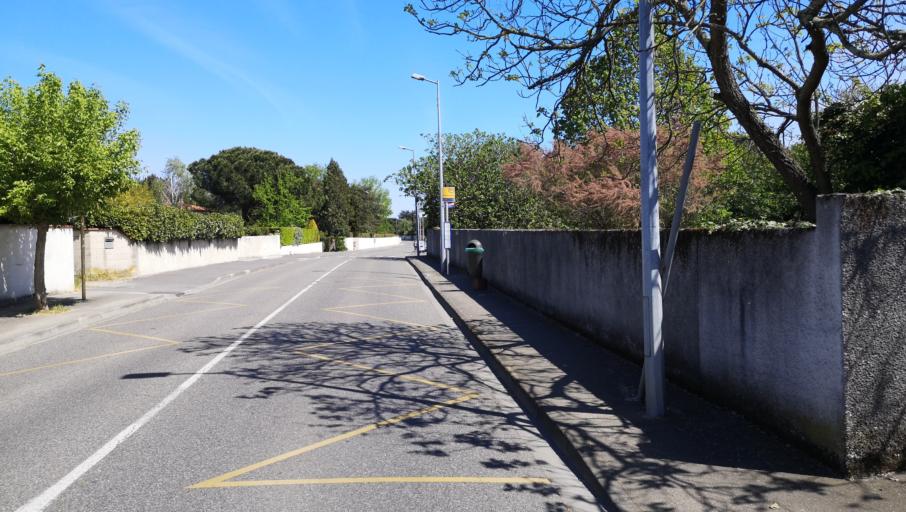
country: FR
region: Midi-Pyrenees
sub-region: Departement de la Haute-Garonne
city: Beauzelle
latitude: 43.6700
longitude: 1.3690
